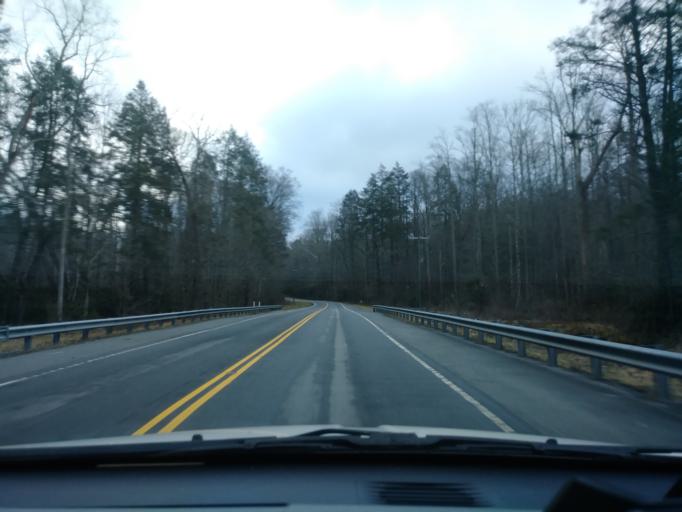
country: US
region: Tennessee
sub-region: Unicoi County
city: Unicoi
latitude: 36.1743
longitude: -82.3024
